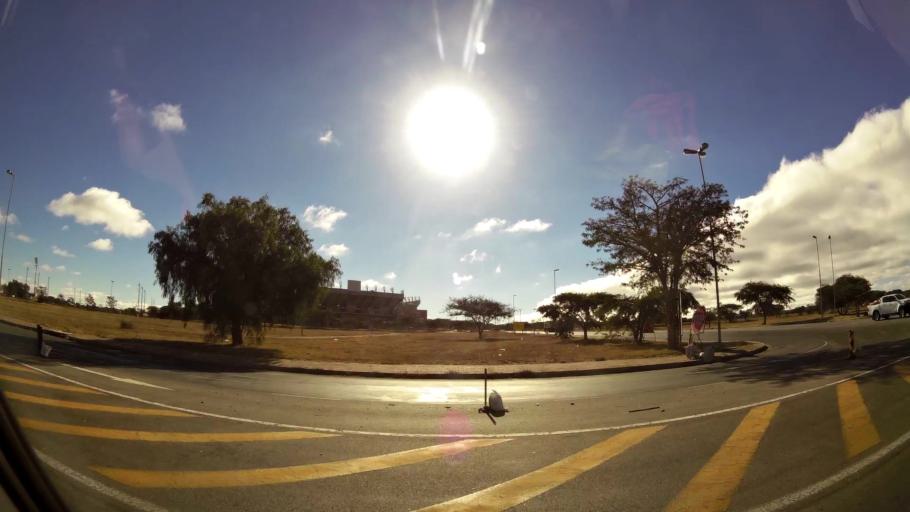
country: ZA
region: Limpopo
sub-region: Capricorn District Municipality
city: Polokwane
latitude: -23.9284
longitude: 29.4665
